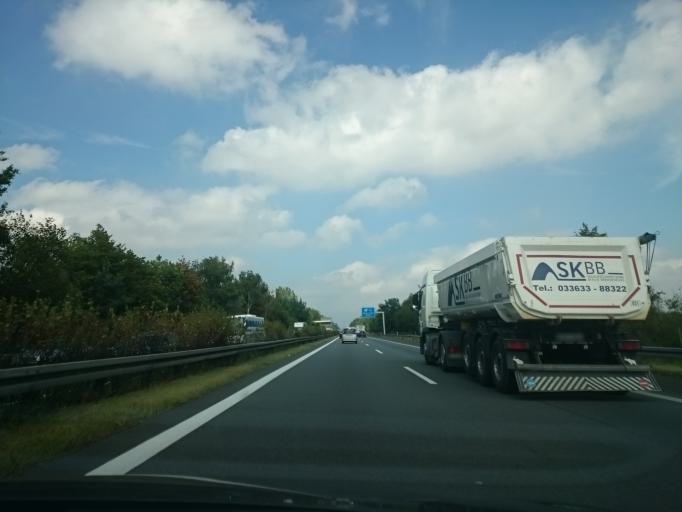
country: DE
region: Brandenburg
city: Bernau bei Berlin
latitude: 52.6377
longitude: 13.5663
